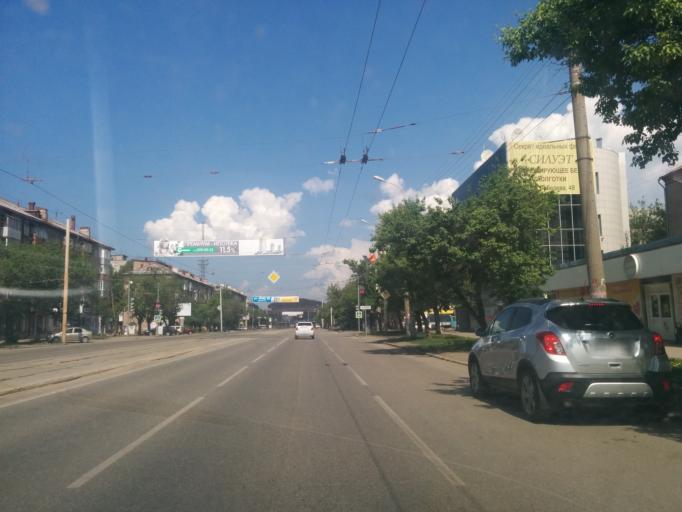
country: RU
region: Perm
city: Perm
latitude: 58.0157
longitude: 56.2806
